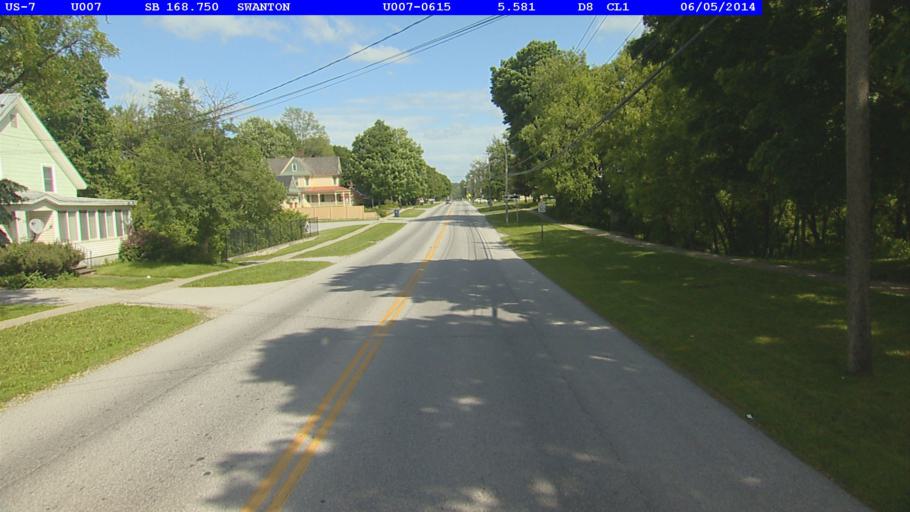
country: US
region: Vermont
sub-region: Franklin County
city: Swanton
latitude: 44.9165
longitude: -73.1214
